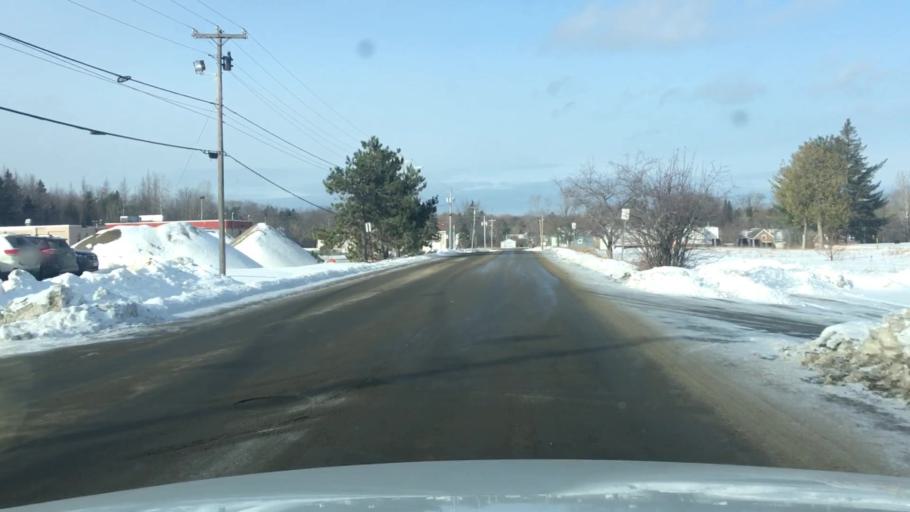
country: US
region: Maine
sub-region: Washington County
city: Calais
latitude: 45.1796
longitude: -67.2670
